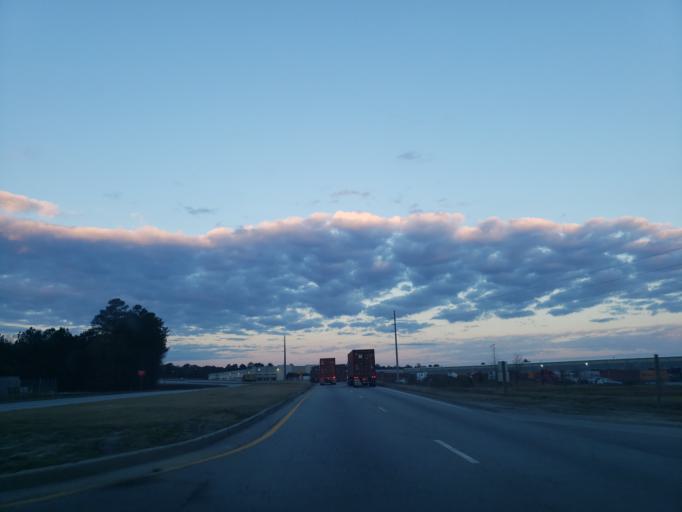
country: US
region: Georgia
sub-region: Chatham County
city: Port Wentworth
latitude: 32.1640
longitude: -81.1938
